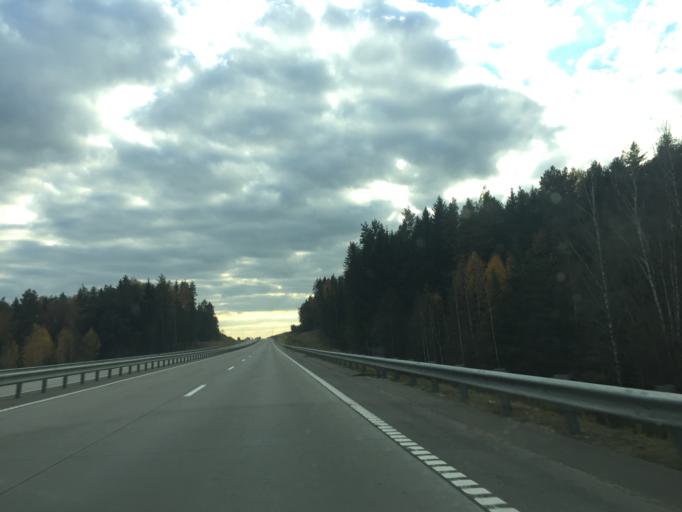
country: BY
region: Minsk
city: Rakaw
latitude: 53.9891
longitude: 27.1087
